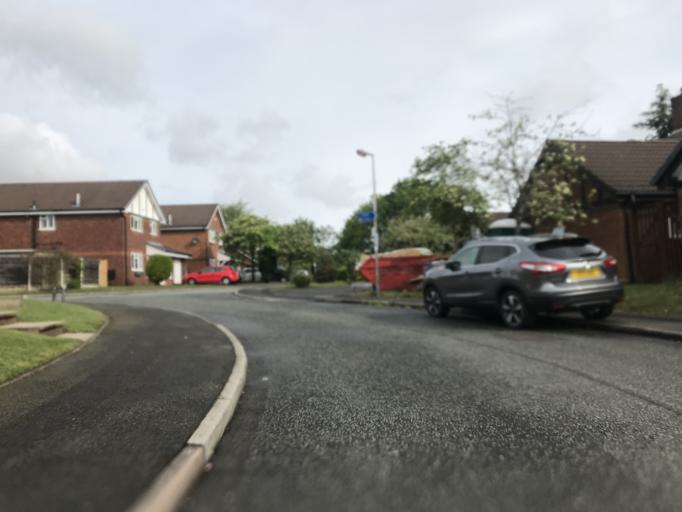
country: GB
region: England
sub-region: Borough of Stockport
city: Cheadle Heath
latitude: 53.4145
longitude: -2.1844
